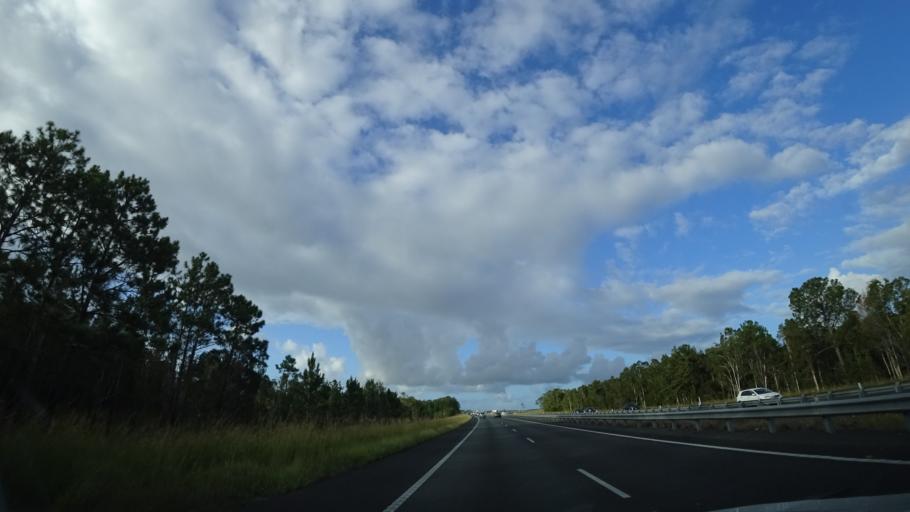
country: AU
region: Queensland
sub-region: Sunshine Coast
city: Little Mountain
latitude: -26.8435
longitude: 153.0308
